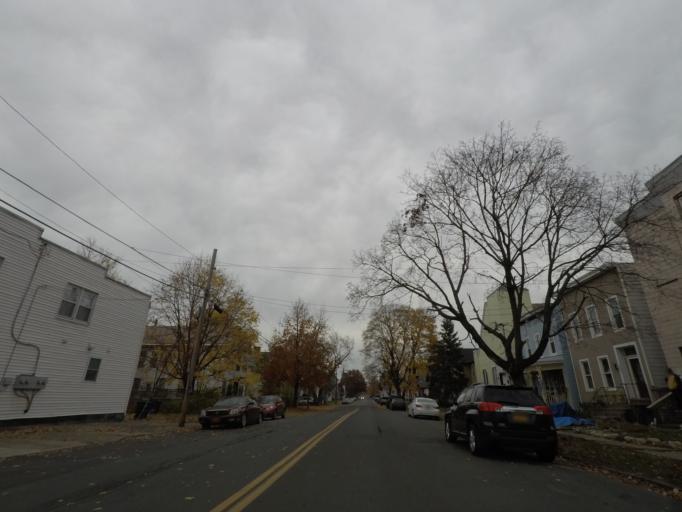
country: US
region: New York
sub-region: Saratoga County
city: Waterford
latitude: 42.7804
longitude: -73.6733
